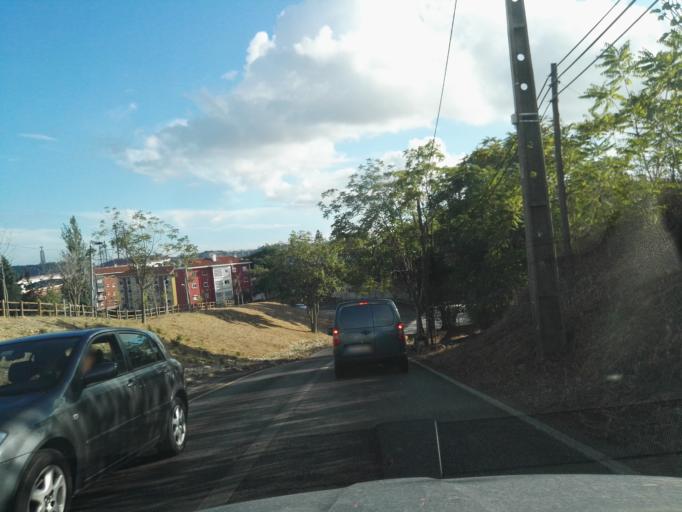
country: PT
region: Setubal
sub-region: Almada
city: Pragal
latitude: 38.7114
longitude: -9.1800
